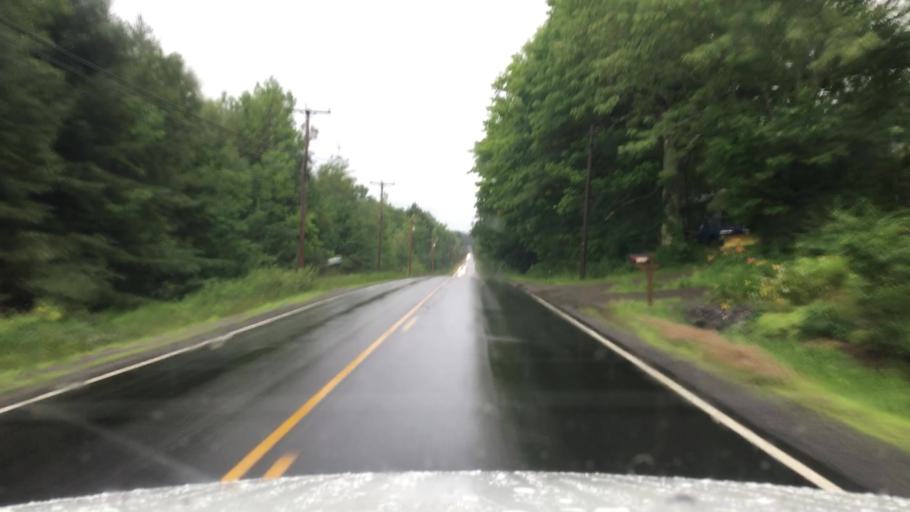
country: US
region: Maine
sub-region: Kennebec County
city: Manchester
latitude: 44.3212
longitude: -69.8507
